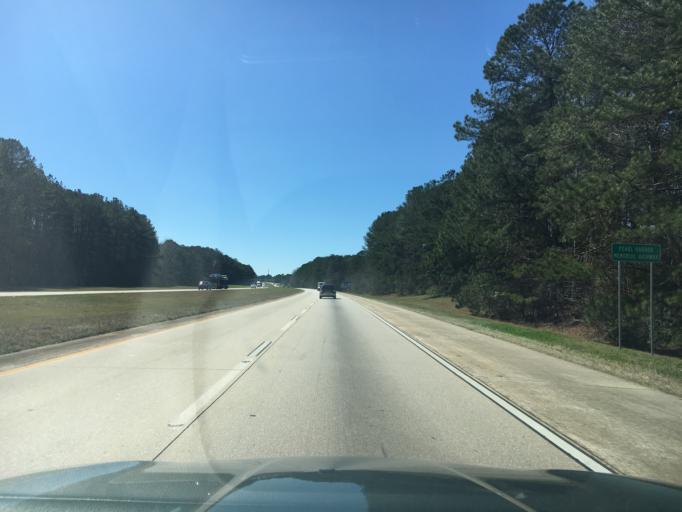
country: US
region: Georgia
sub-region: Troup County
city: La Grange
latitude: 33.0559
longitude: -84.9540
